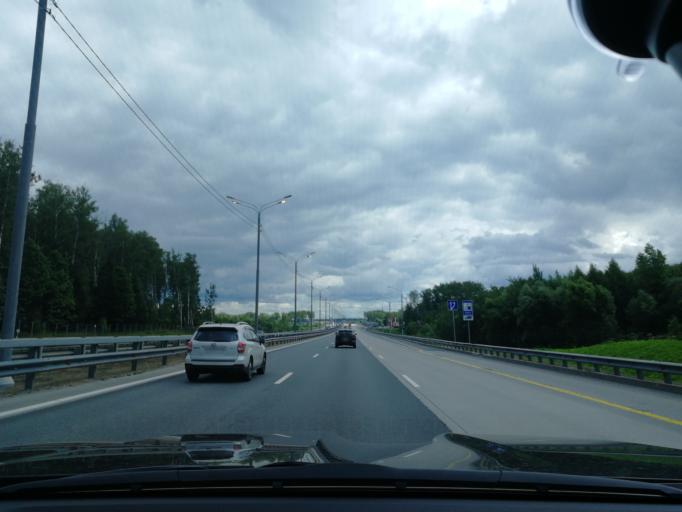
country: RU
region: Moskovskaya
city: Belyye Stolby
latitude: 55.2928
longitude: 37.8471
